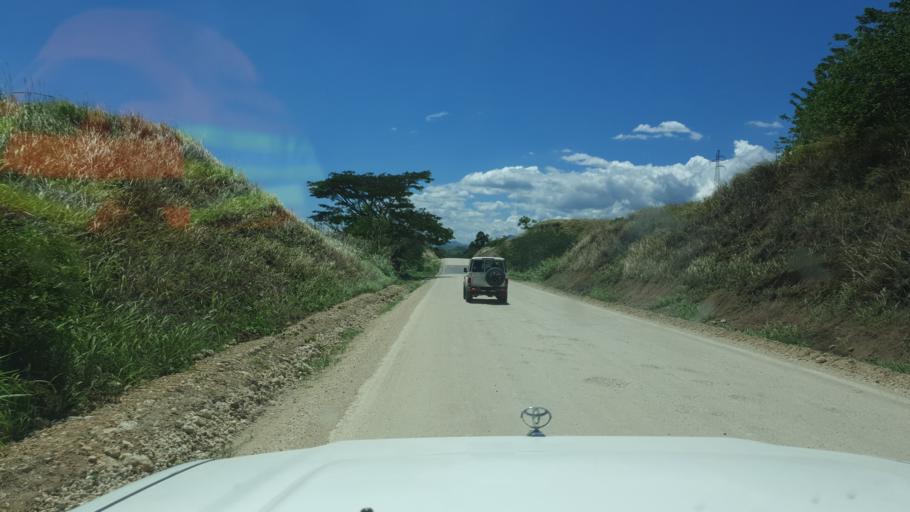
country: PG
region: Eastern Highlands
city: Goroka
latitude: -5.8044
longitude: 145.6281
